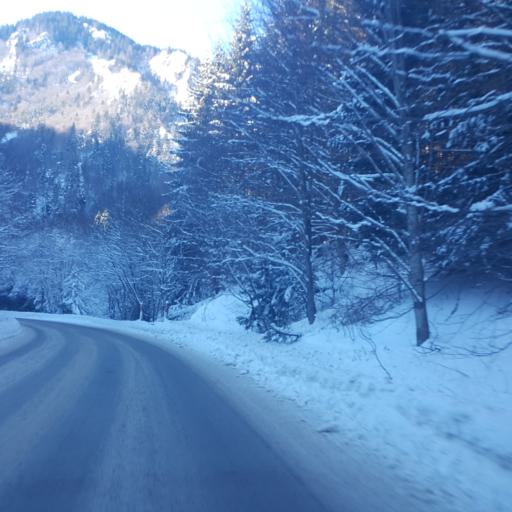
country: XK
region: Mitrovica
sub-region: Komuna e Leposaviqit
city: Leposaviq
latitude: 43.3060
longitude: 20.8604
